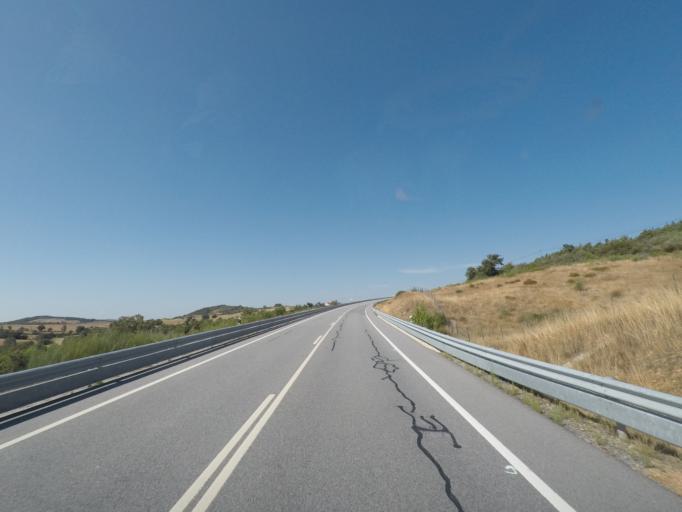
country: PT
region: Braganca
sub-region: Mogadouro
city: Mogadouro
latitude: 41.3451
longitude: -6.6246
